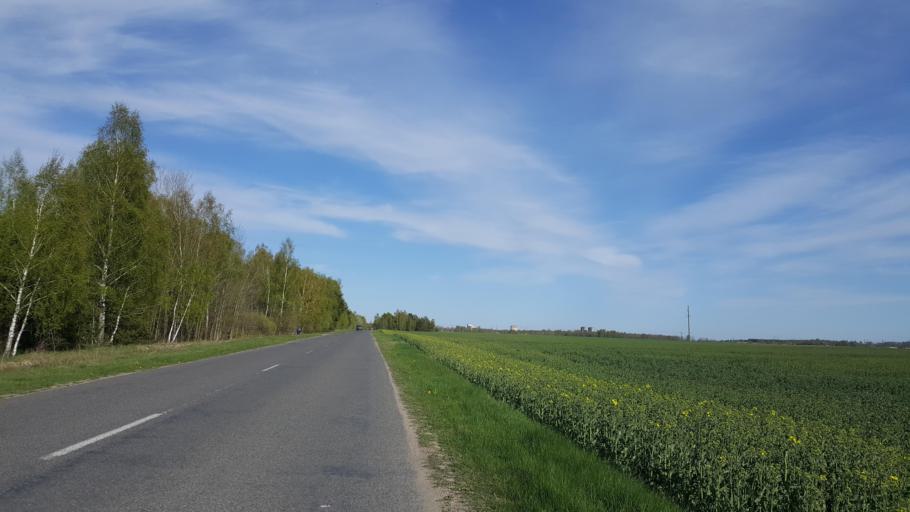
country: BY
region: Brest
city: Vysokaye
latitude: 52.4015
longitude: 23.4701
